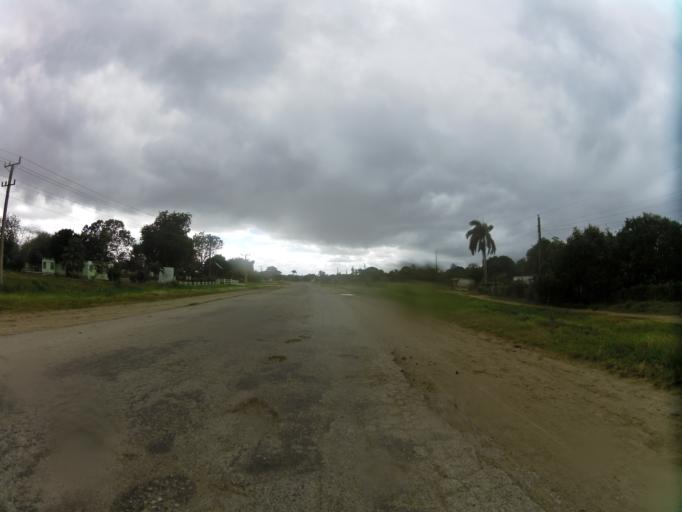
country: CU
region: Las Tunas
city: Las Tunas
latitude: 21.0454
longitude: -76.9325
